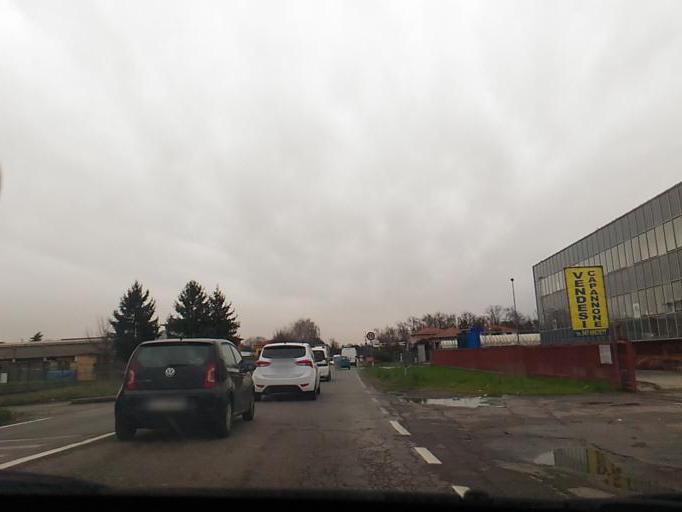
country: IT
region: Lombardy
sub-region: Provincia di Como
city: Figino Serenza
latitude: 45.7008
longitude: 9.1408
